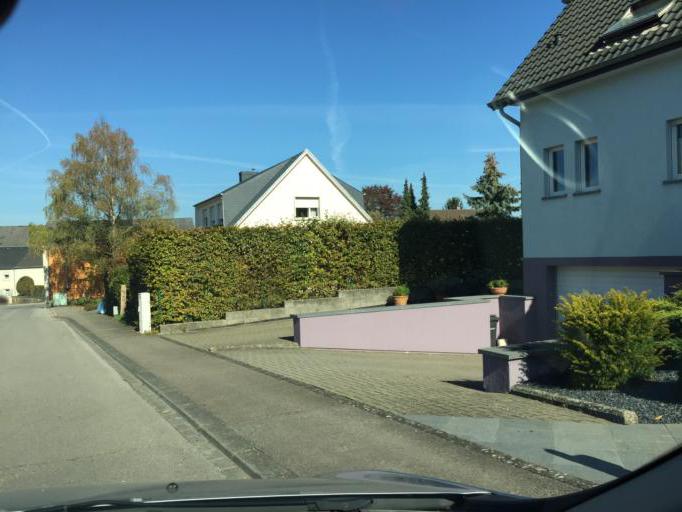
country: LU
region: Luxembourg
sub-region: Canton de Luxembourg
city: Contern
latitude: 49.5840
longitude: 6.2288
